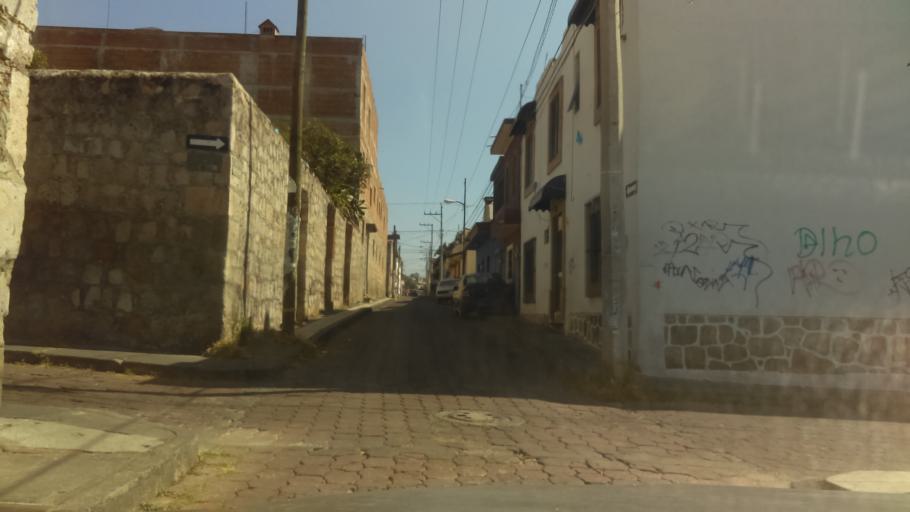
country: MX
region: Michoacan
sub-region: Morelia
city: Montana Monarca (Punta Altozano)
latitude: 19.6721
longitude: -101.1912
